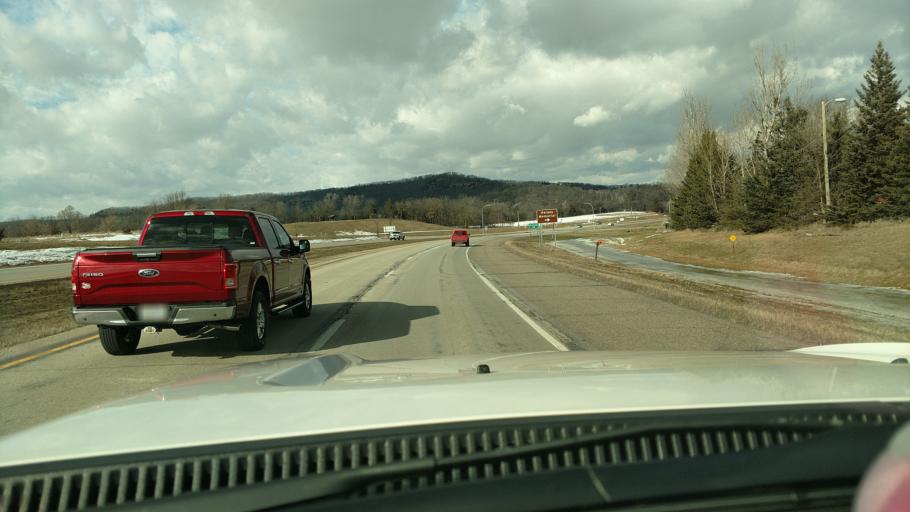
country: US
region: Minnesota
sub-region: Wabasha County
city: Wabasha
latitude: 44.3048
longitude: -92.0047
